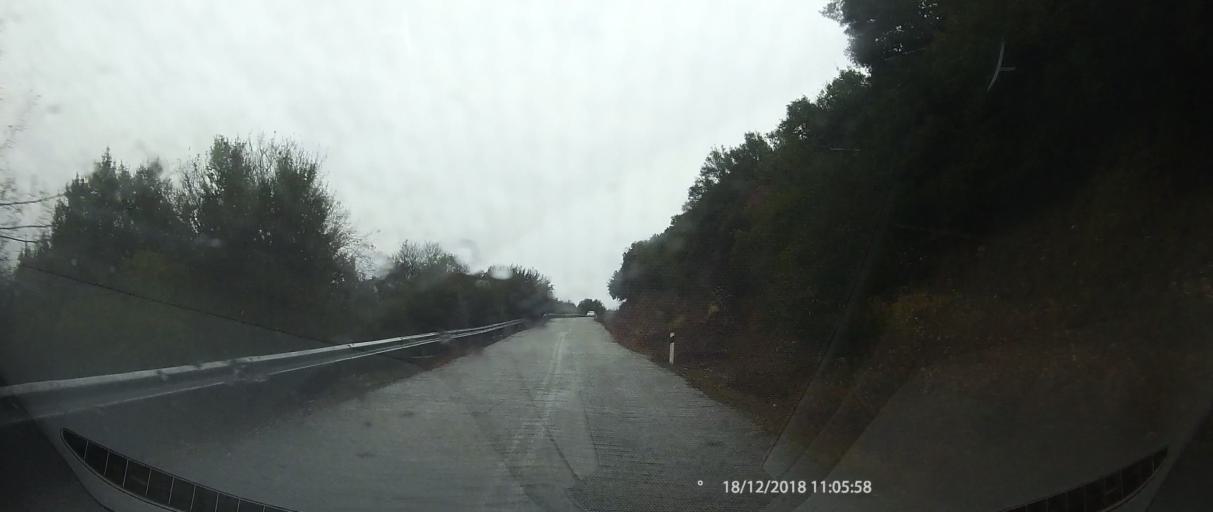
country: GR
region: Central Macedonia
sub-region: Nomos Pierias
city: Kato Milia
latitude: 40.2170
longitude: 22.3233
